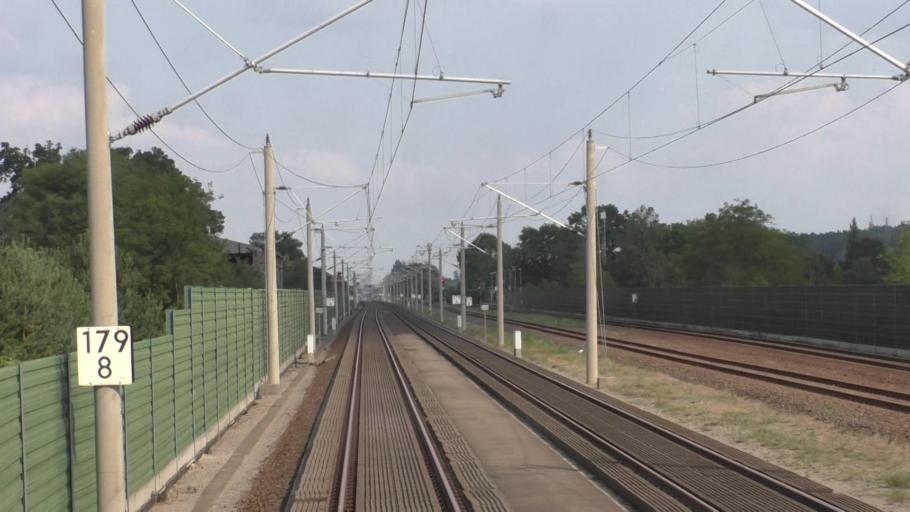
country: DE
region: Saxony-Anhalt
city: Schollene
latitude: 52.5906
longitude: 12.2237
